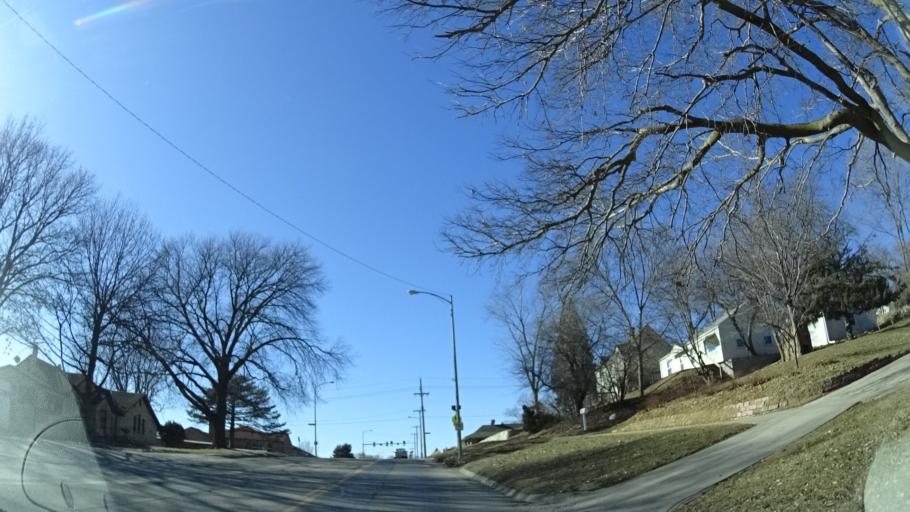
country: US
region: Nebraska
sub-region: Sarpy County
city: Bellevue
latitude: 41.1366
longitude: -95.9032
